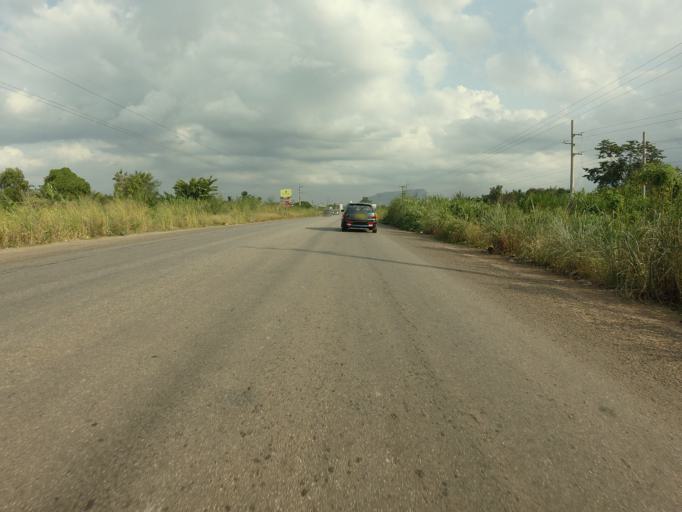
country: GH
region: Volta
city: Ho
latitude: 6.5867
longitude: 0.4794
